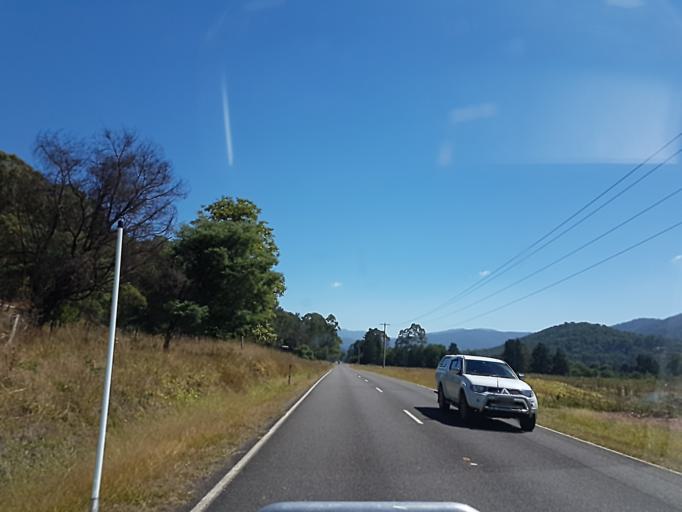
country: AU
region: Victoria
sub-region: Alpine
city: Mount Beauty
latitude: -36.7824
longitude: 147.0356
